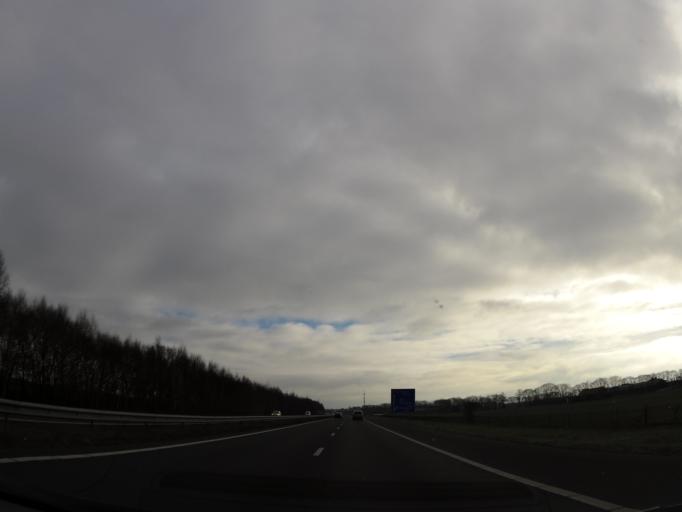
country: NL
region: North Brabant
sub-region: Gemeente Boxmeer
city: Overloon
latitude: 51.5926
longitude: 5.9752
